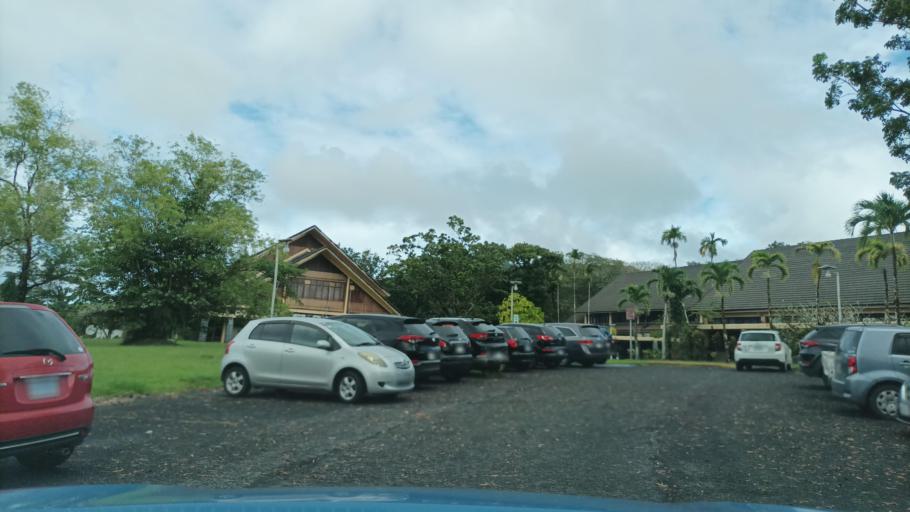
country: FM
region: Pohnpei
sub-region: Sokehs Municipality
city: Palikir - National Government Center
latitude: 6.9238
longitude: 158.1597
